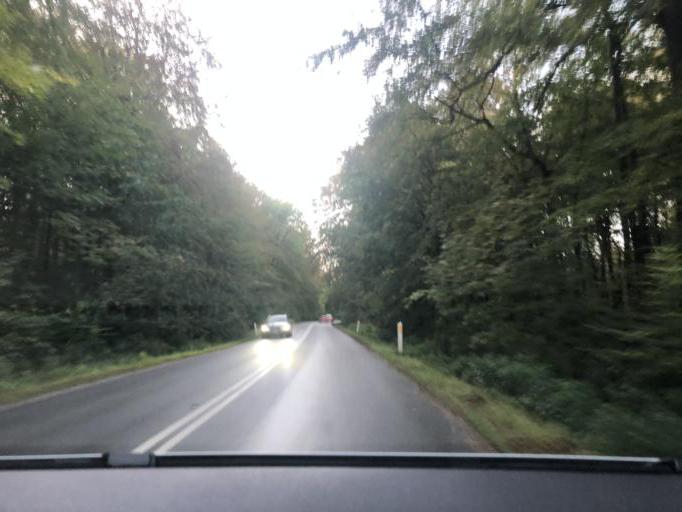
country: DK
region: Capital Region
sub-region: Frederikssund Kommune
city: Slangerup
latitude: 55.8149
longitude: 12.2049
